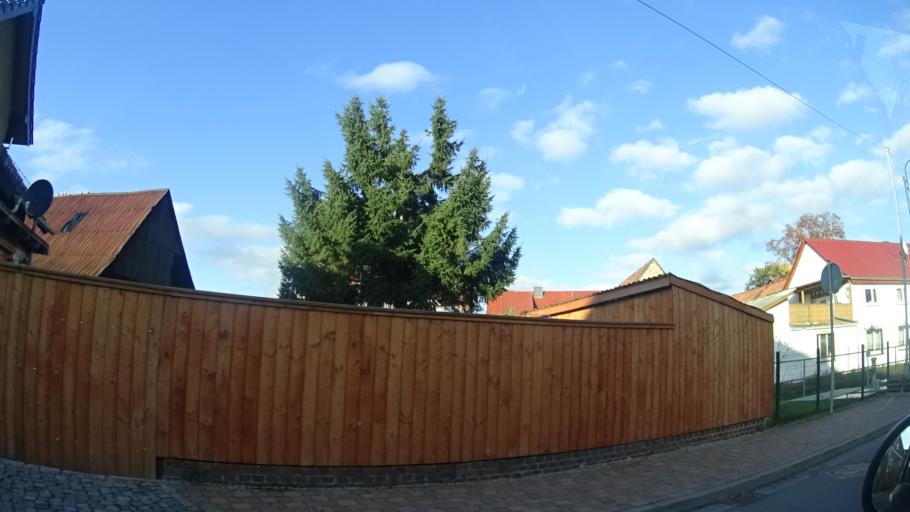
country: DE
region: Thuringia
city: Dornheim
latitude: 50.8349
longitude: 10.9934
